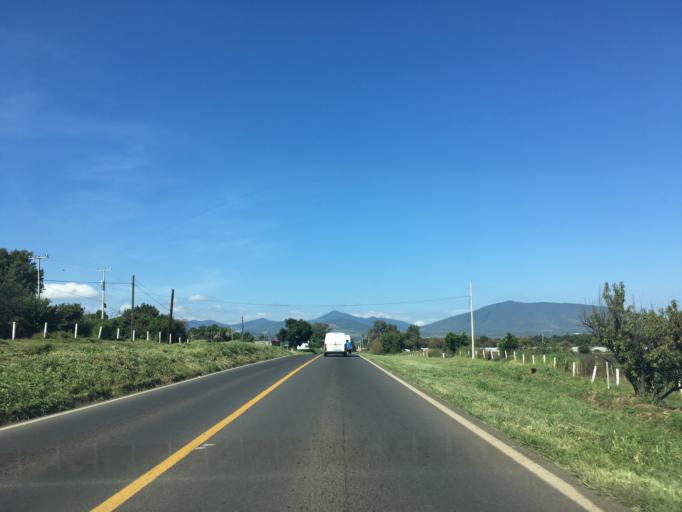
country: MX
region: Mexico
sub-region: Chalco
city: Los Nogales
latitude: 19.8620
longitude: -102.1715
